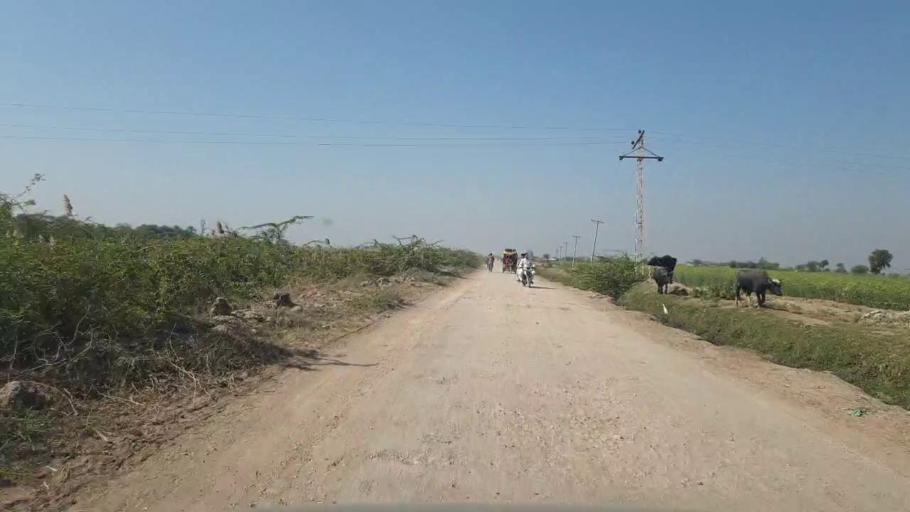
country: PK
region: Sindh
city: Samaro
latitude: 25.2811
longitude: 69.2401
